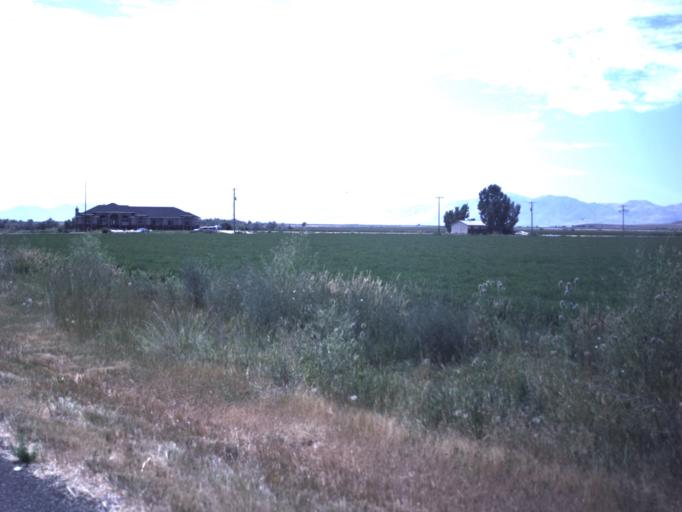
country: US
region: Utah
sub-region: Box Elder County
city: Tremonton
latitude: 41.6525
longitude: -112.2958
